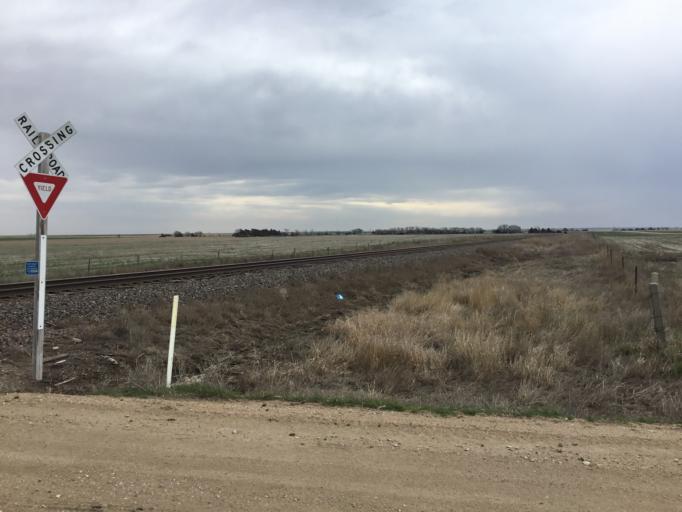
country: US
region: Kansas
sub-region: Russell County
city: Russell
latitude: 38.8867
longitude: -98.9654
